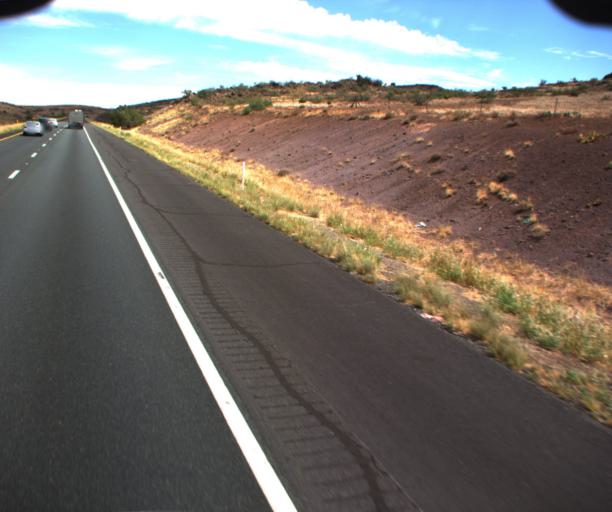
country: US
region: Arizona
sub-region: Yavapai County
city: Cordes Lakes
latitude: 34.4538
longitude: -112.0305
